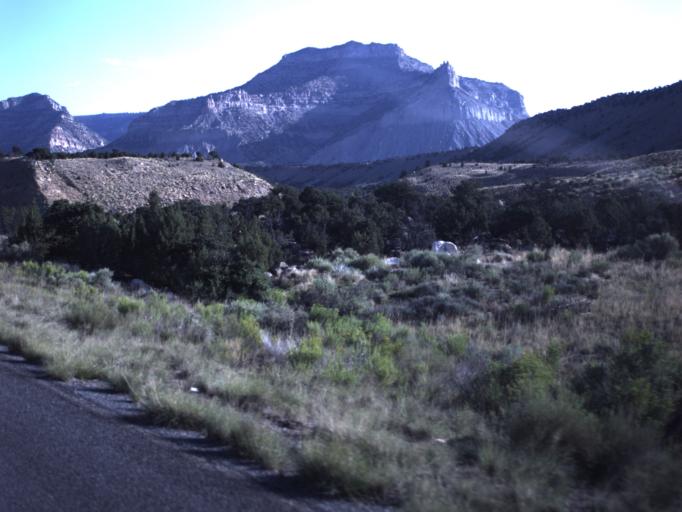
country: US
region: Utah
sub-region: Emery County
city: Huntington
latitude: 39.3636
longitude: -111.0486
